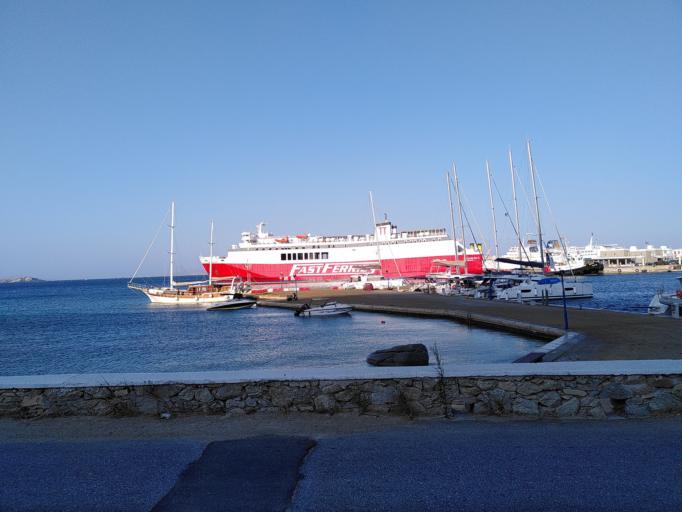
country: GR
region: South Aegean
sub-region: Nomos Kykladon
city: Mykonos
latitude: 37.4635
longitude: 25.3286
